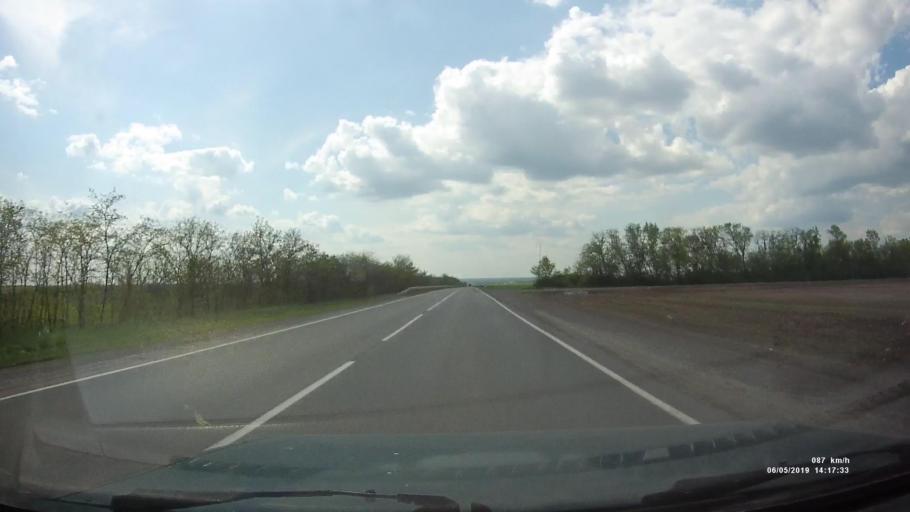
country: RU
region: Rostov
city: Kamenolomni
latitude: 47.6339
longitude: 40.2663
